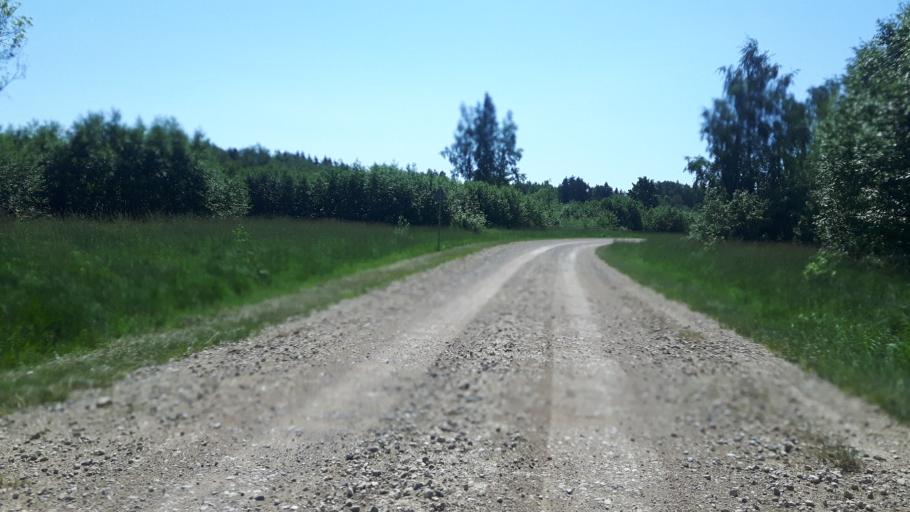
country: EE
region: Paernumaa
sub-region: Vaendra vald (alev)
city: Vandra
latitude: 58.5613
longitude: 24.9528
